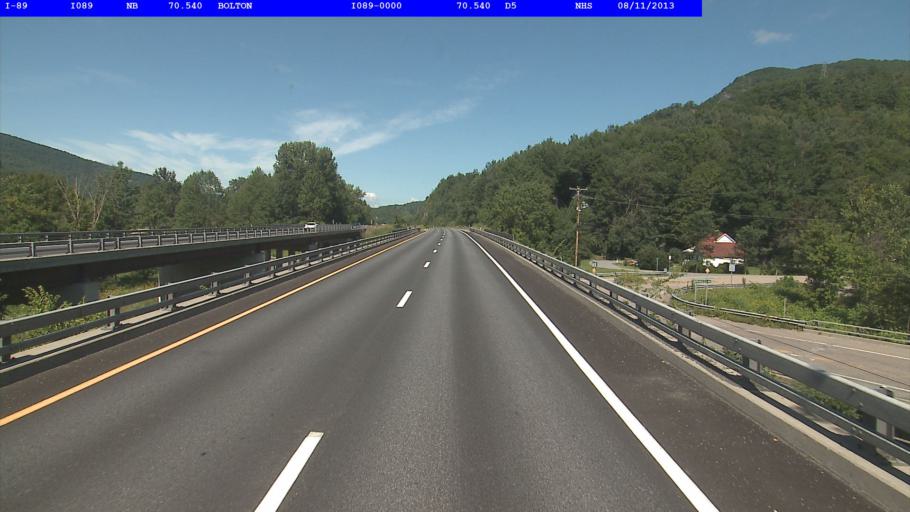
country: US
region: Vermont
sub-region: Washington County
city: Waterbury
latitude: 44.3729
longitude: -72.8781
